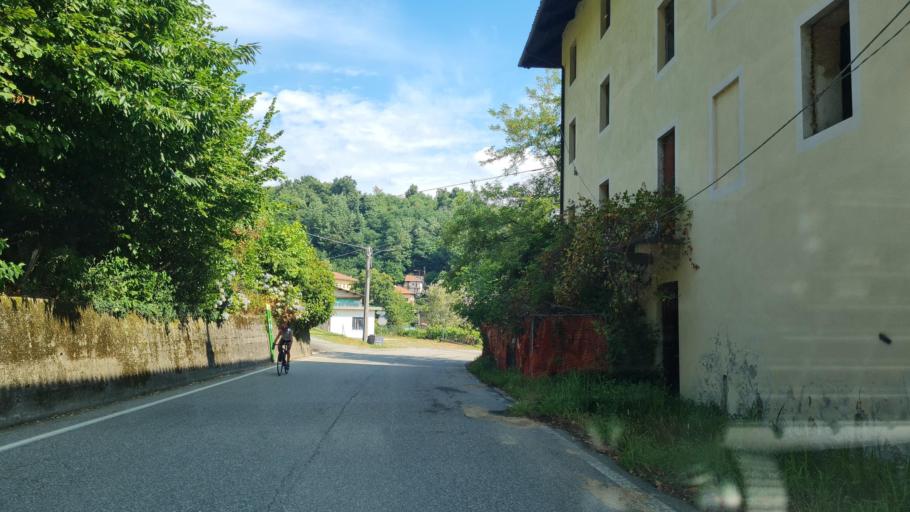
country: IT
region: Piedmont
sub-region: Provincia di Biella
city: Fontanella-Ozino
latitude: 45.6184
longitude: 8.1566
